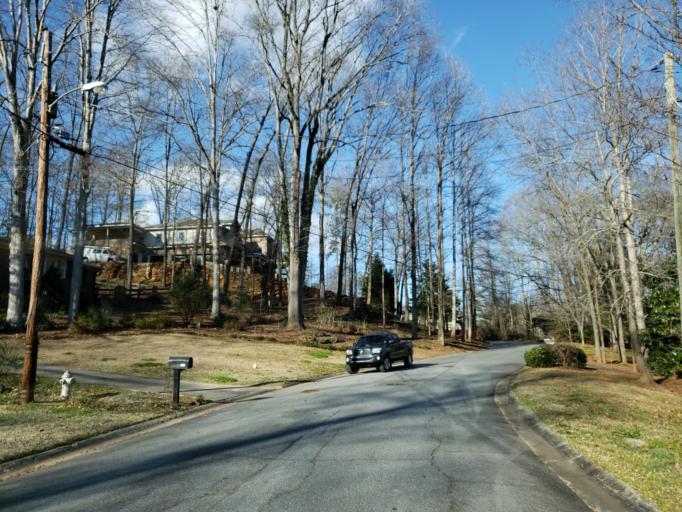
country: US
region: Georgia
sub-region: Cherokee County
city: Woodstock
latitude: 34.0339
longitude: -84.4891
